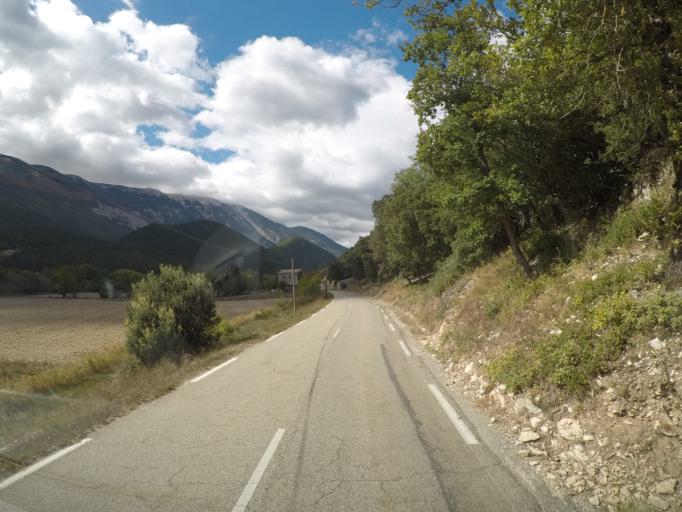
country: FR
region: Provence-Alpes-Cote d'Azur
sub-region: Departement du Vaucluse
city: Sault
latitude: 44.1837
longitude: 5.3652
